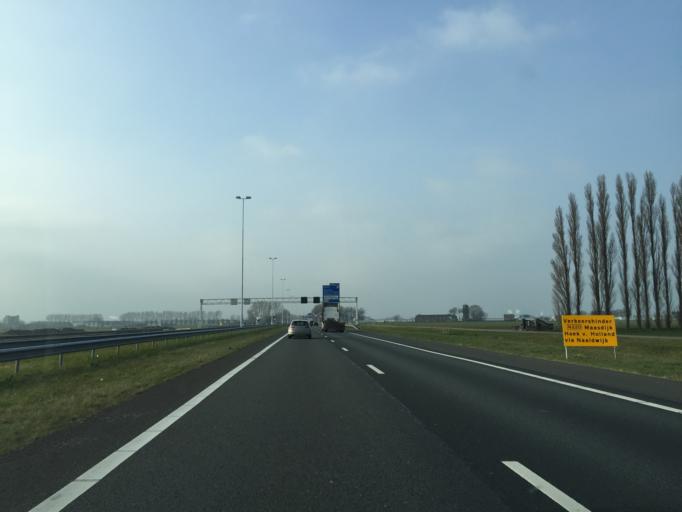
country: NL
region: South Holland
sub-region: Gemeente Maassluis
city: Maassluis
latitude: 51.9379
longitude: 4.2473
